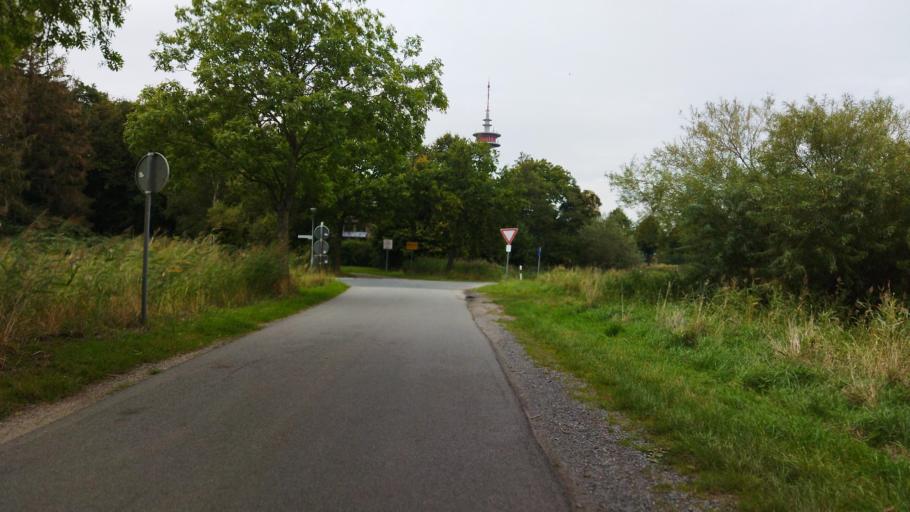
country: DE
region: Lower Saxony
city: Leer
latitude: 53.2588
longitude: 7.4371
